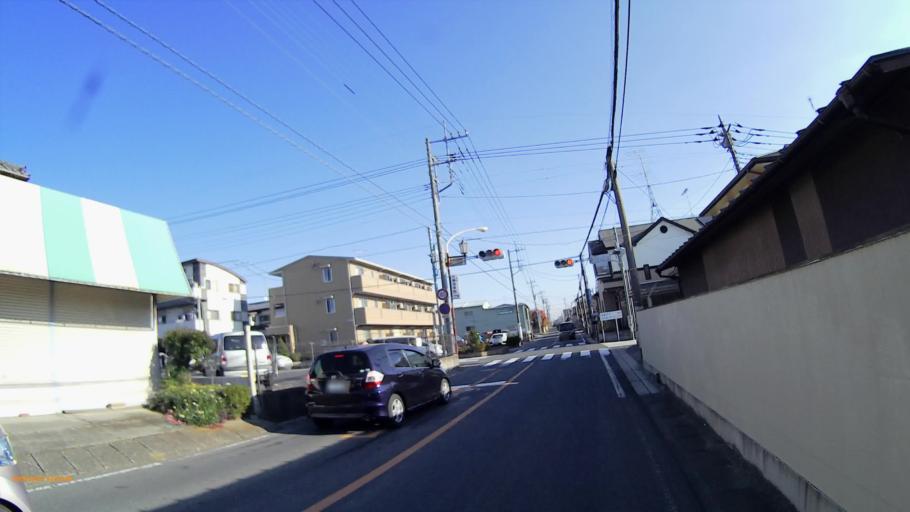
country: JP
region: Saitama
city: Konosu
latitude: 36.0713
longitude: 139.4940
